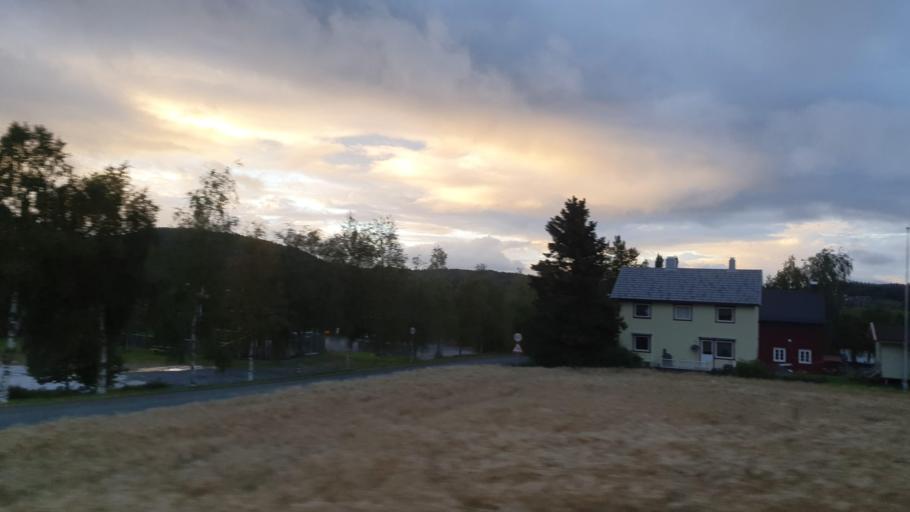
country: NO
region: Nord-Trondelag
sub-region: Levanger
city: Skogn
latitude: 63.6753
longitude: 11.1277
